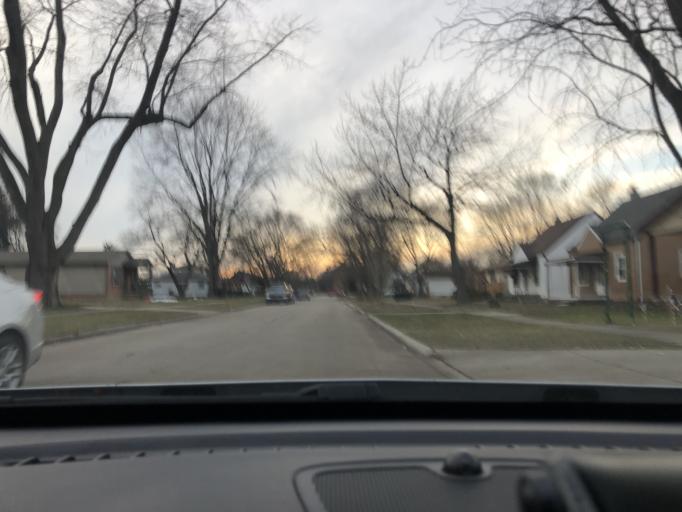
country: US
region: Michigan
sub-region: Wayne County
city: Allen Park
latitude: 42.2735
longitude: -83.2365
